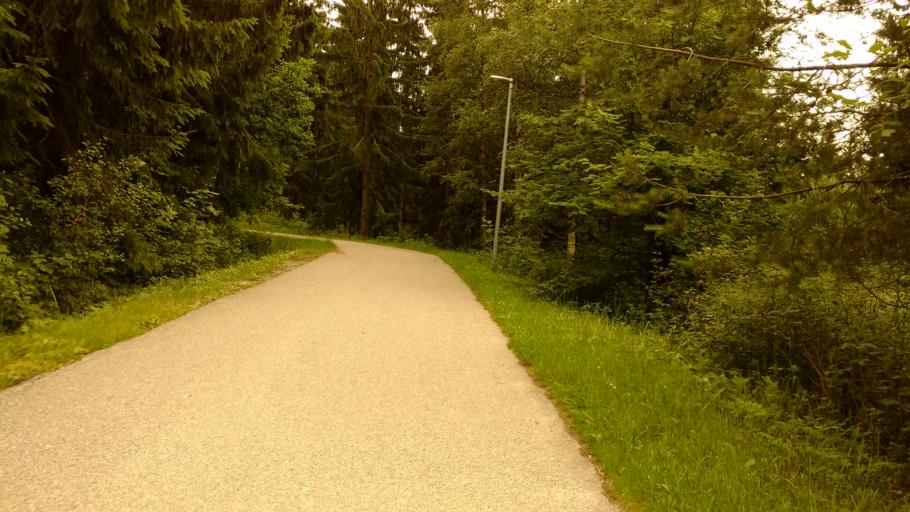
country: FI
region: Varsinais-Suomi
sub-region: Salo
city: Salo
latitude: 60.4022
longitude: 23.1743
